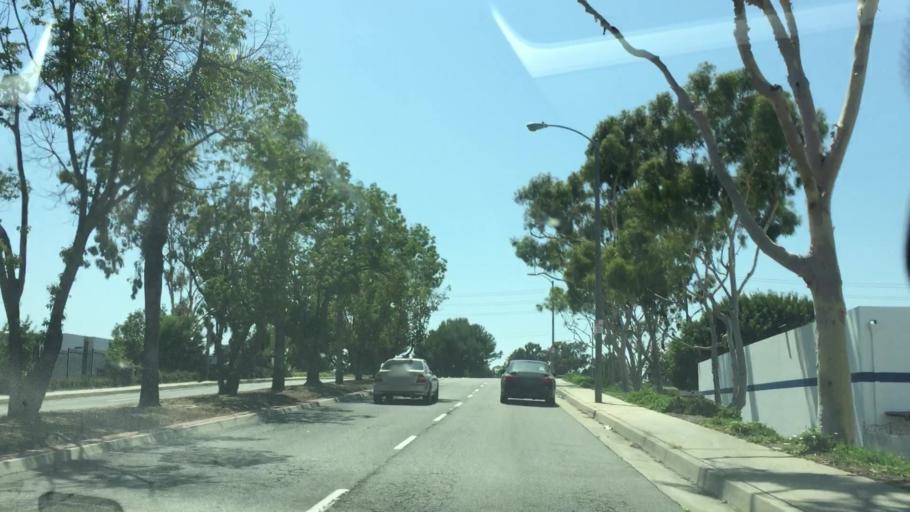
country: US
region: California
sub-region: Orange County
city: Fountain Valley
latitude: 33.7087
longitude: -117.9232
